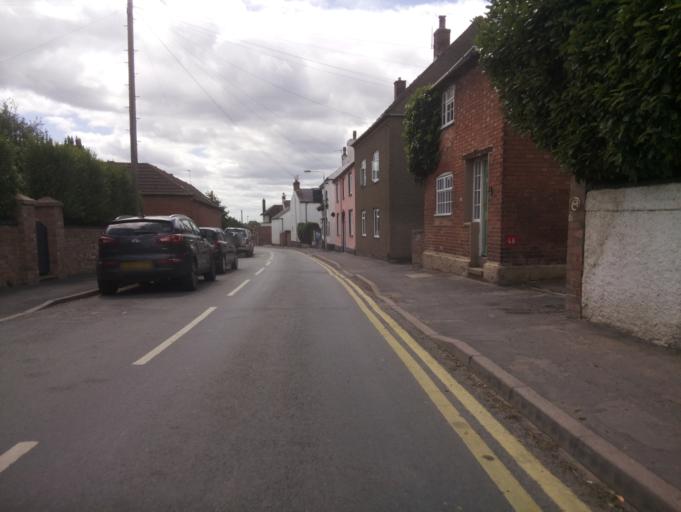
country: GB
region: England
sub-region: Nottinghamshire
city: Ruddington
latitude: 52.8688
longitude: -1.0901
